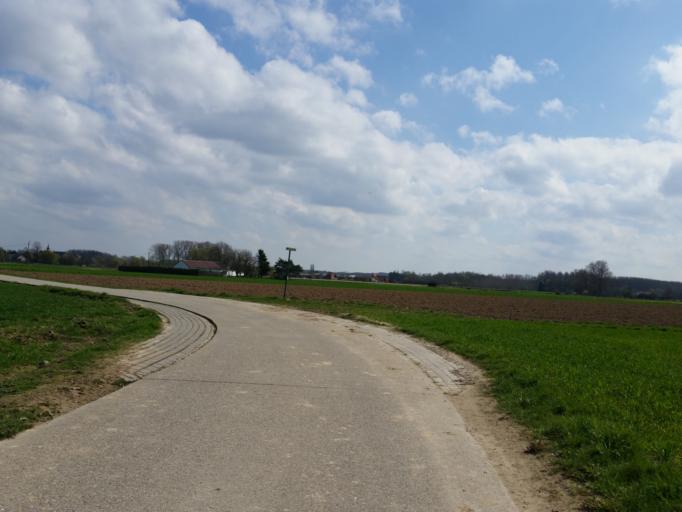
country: BE
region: Flanders
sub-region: Provincie Vlaams-Brabant
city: Haacht
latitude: 50.9428
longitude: 4.6056
